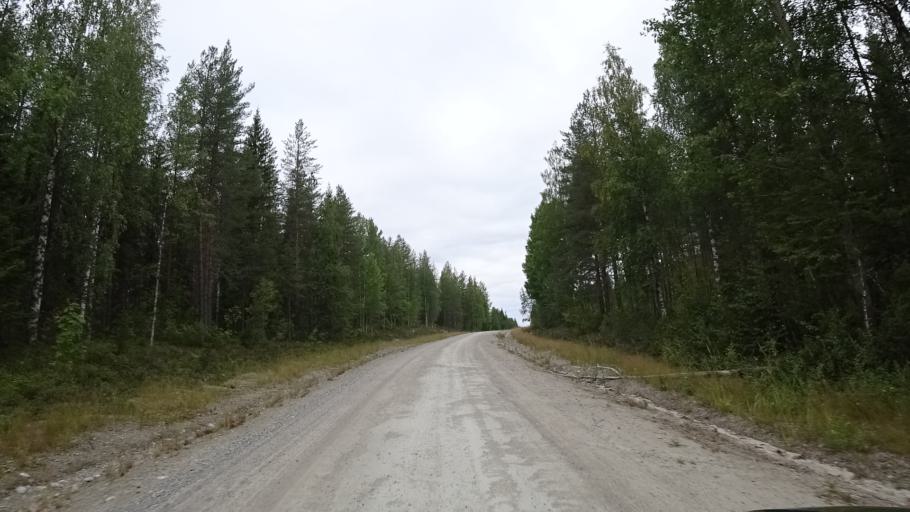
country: FI
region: North Karelia
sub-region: Joensuu
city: Eno
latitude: 63.1541
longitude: 30.6140
